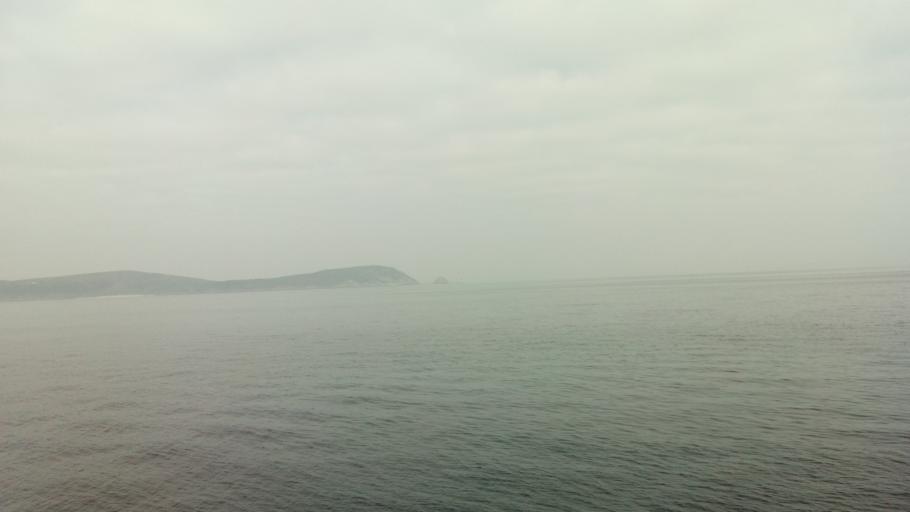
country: ES
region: Galicia
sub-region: Provincia de Pontevedra
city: Sanxenxo
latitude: 42.3795
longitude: -8.8923
